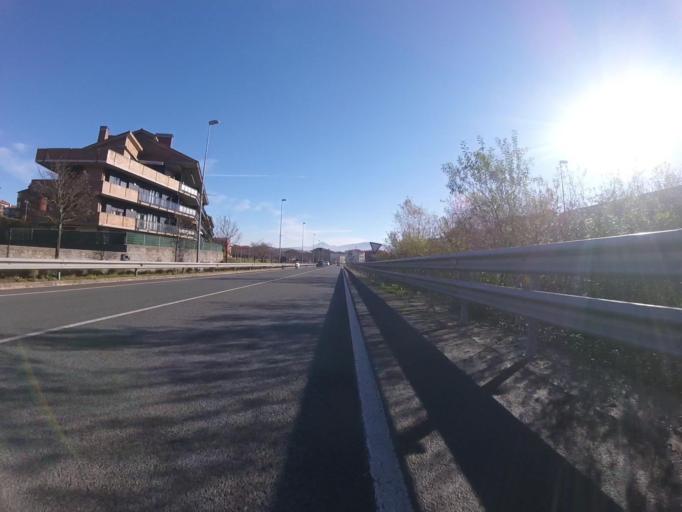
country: ES
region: Basque Country
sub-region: Provincia de Guipuzcoa
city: Fuenterrabia
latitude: 43.3620
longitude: -1.7971
